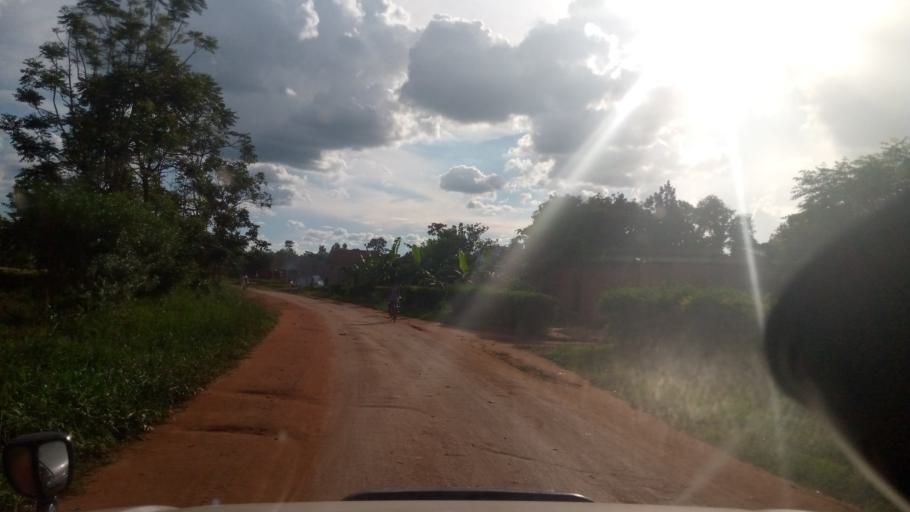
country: UG
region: Northern Region
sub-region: Lira District
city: Lira
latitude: 2.2288
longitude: 32.9005
